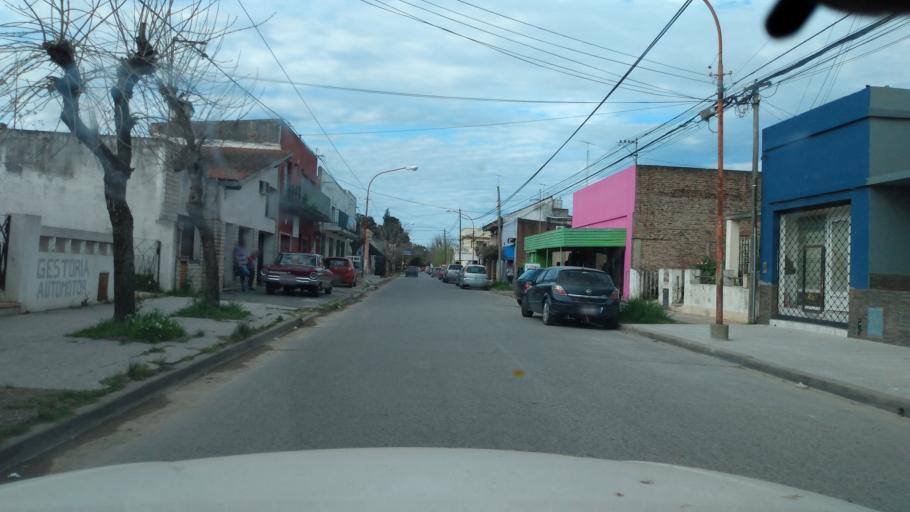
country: AR
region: Buenos Aires
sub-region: Partido de Lujan
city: Lujan
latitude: -34.5674
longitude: -59.1314
